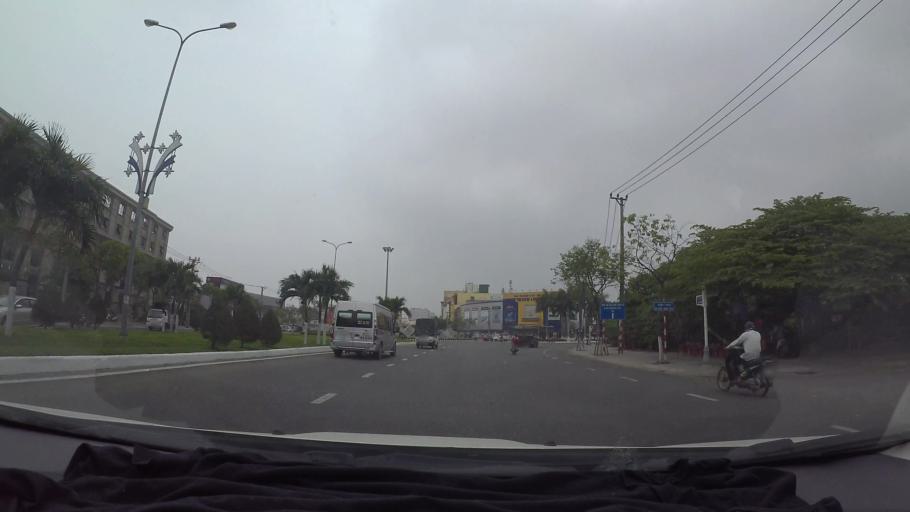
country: VN
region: Da Nang
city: Cam Le
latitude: 16.0305
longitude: 108.2090
